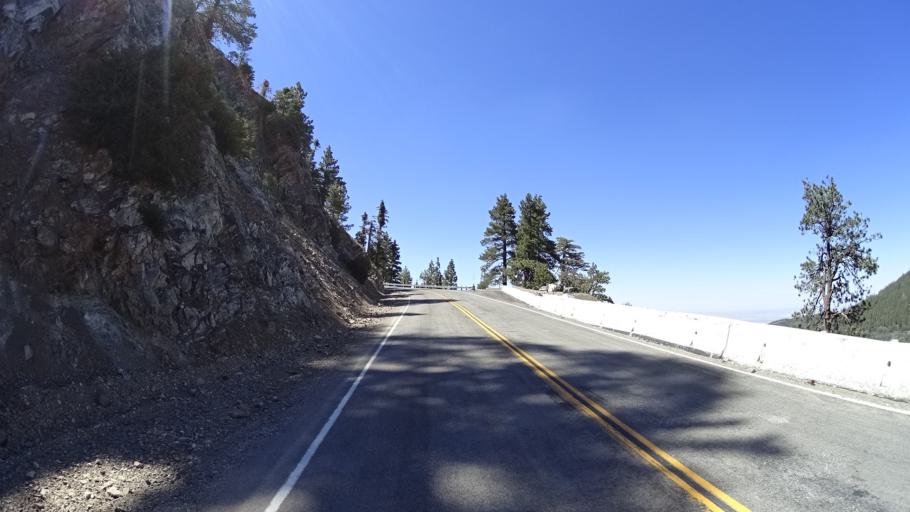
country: US
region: California
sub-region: San Bernardino County
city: Pinon Hills
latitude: 34.3751
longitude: -117.7679
